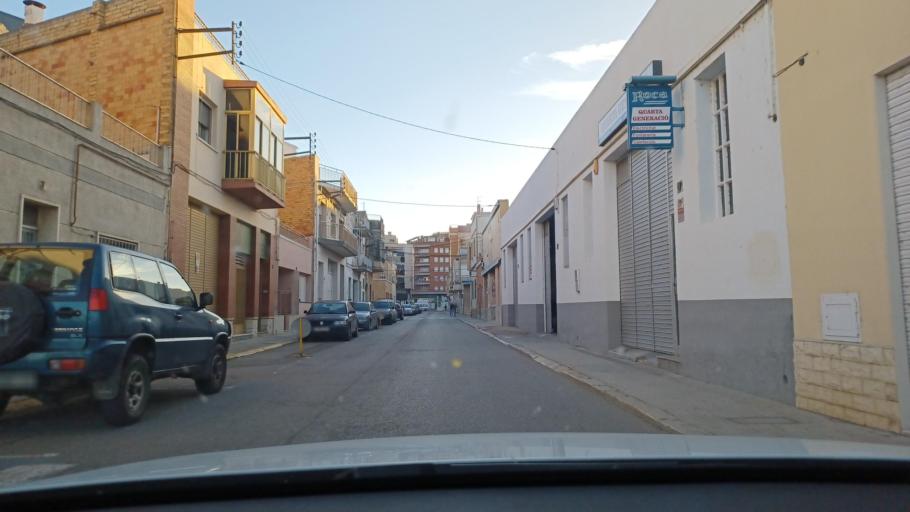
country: ES
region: Catalonia
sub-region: Provincia de Tarragona
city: Amposta
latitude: 40.7124
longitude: 0.5832
